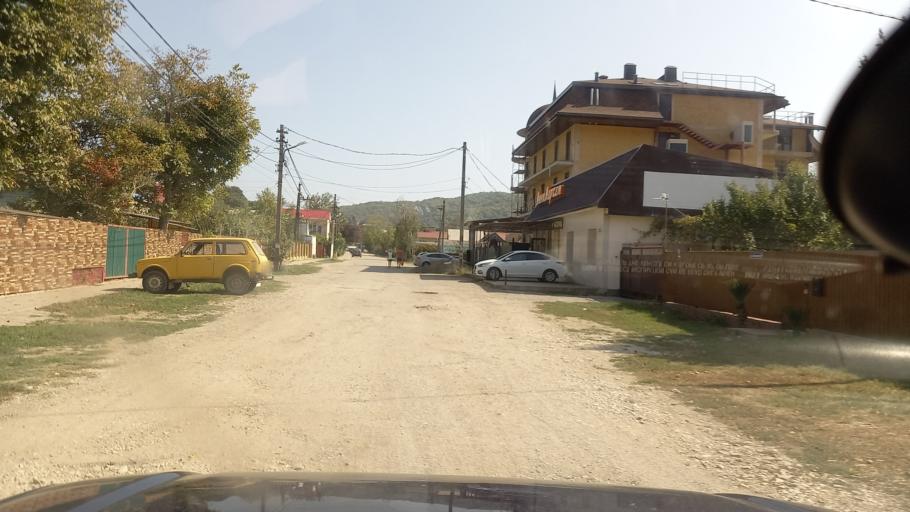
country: RU
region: Krasnodarskiy
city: Arkhipo-Osipovka
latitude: 44.3651
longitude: 38.5243
